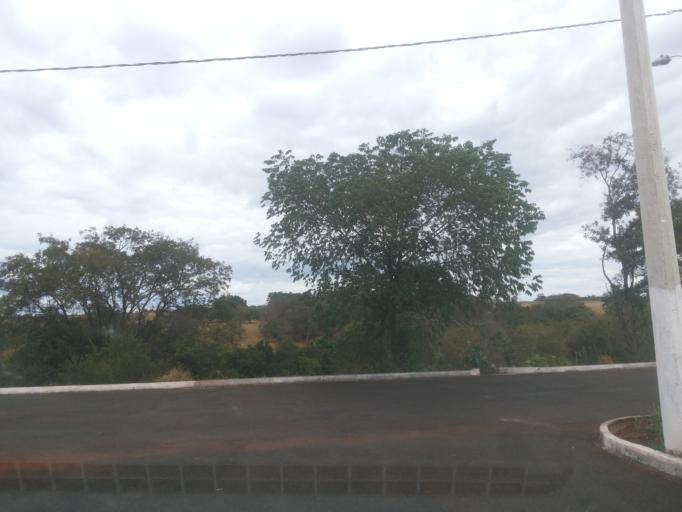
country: BR
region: Minas Gerais
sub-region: Centralina
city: Centralina
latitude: -18.7326
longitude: -49.2024
